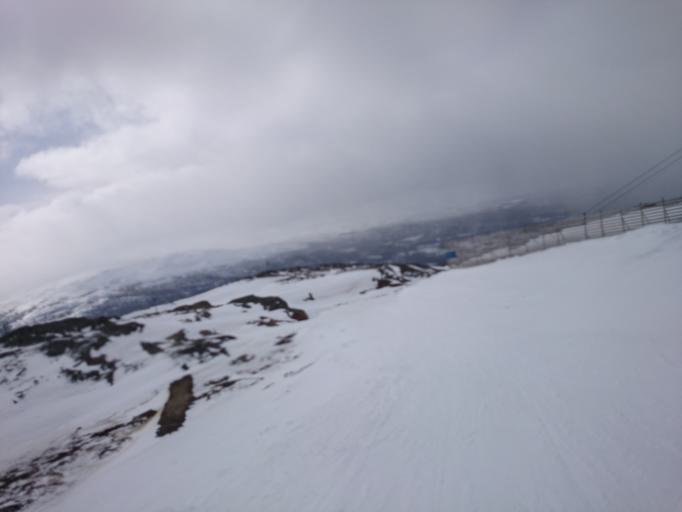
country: SE
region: Jaemtland
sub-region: Are Kommun
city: Are
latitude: 63.4136
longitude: 13.0813
